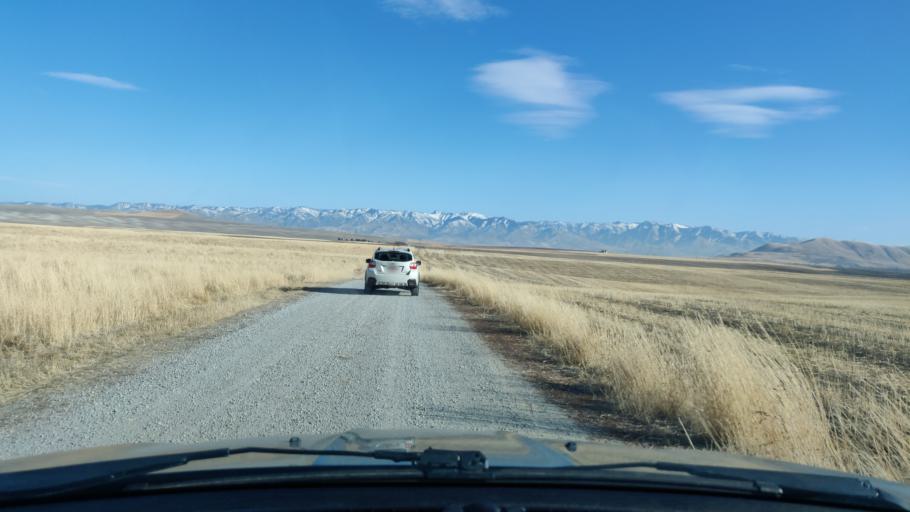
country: US
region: Utah
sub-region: Cache County
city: Benson
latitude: 41.9314
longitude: -112.0390
